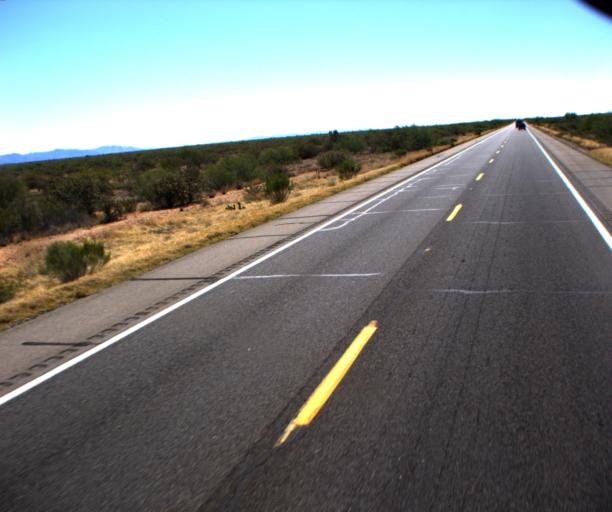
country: US
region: Arizona
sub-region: Yavapai County
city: Congress
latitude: 34.1647
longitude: -113.0100
